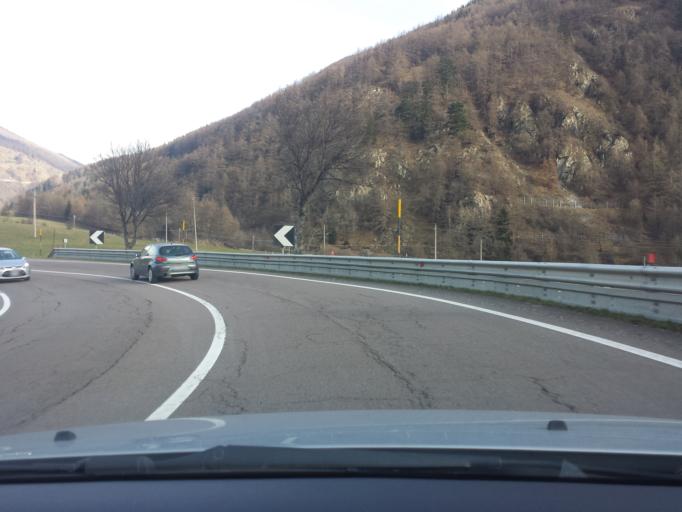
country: IT
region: Trentino-Alto Adige
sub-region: Bolzano
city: Malles Venosta
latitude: 46.7040
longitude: 10.5401
